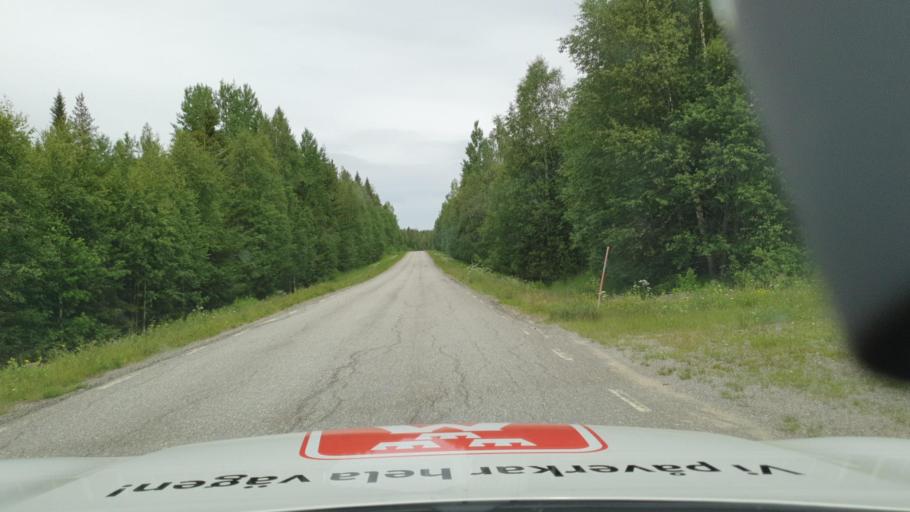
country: SE
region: Vaesterbotten
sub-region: Robertsfors Kommun
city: Robertsfors
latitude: 64.2902
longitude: 20.6479
